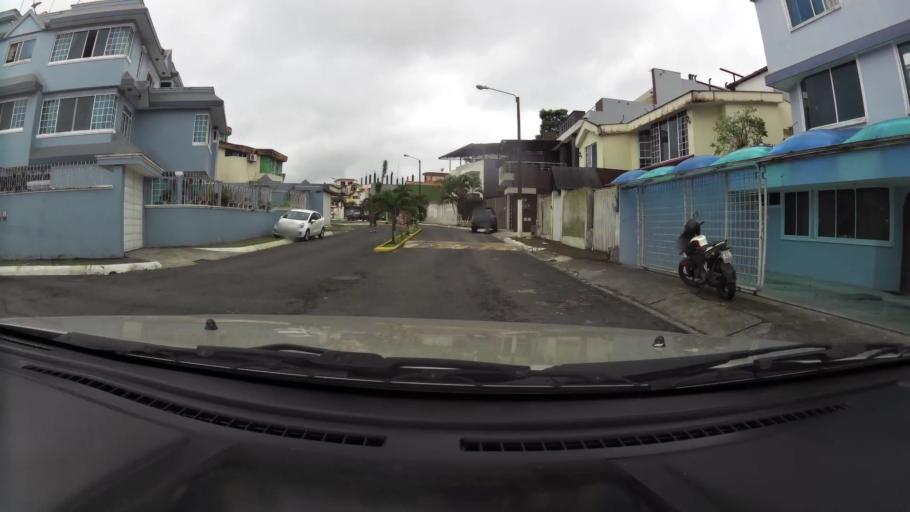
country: EC
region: Santo Domingo de los Tsachilas
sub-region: Canton Santo Domingo de los Colorados
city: Santo Domingo de los Colorados
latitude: -0.2536
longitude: -79.1576
